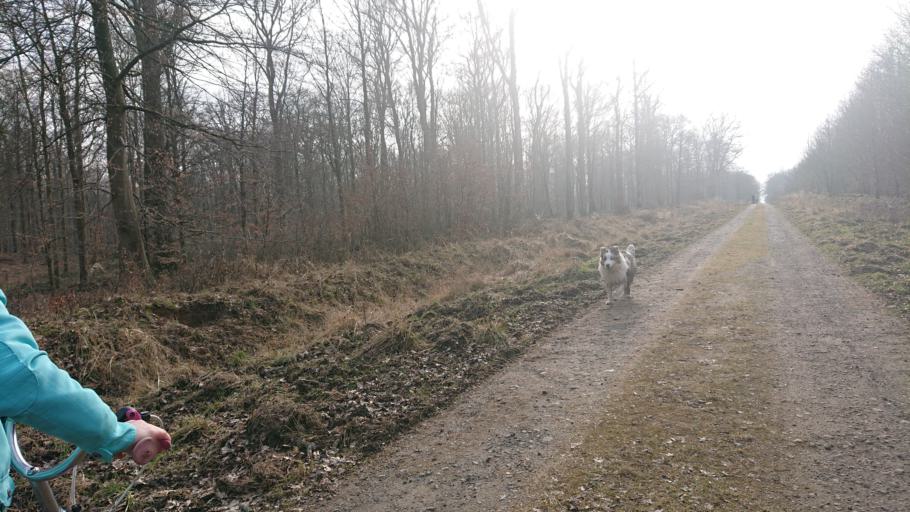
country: FR
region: Nord-Pas-de-Calais
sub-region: Departement du Nord
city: Landrecies
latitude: 50.1686
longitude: 3.7133
